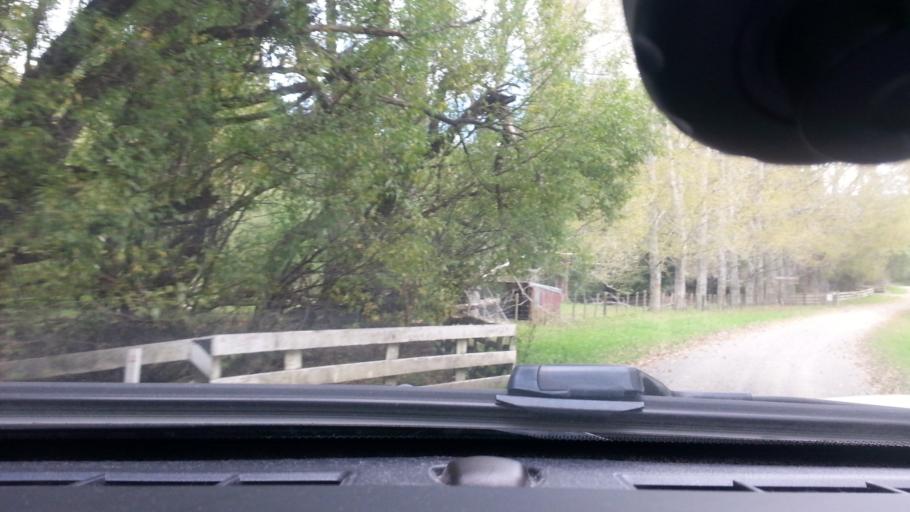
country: NZ
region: Wellington
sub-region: Masterton District
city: Masterton
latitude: -40.7848
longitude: 175.8414
